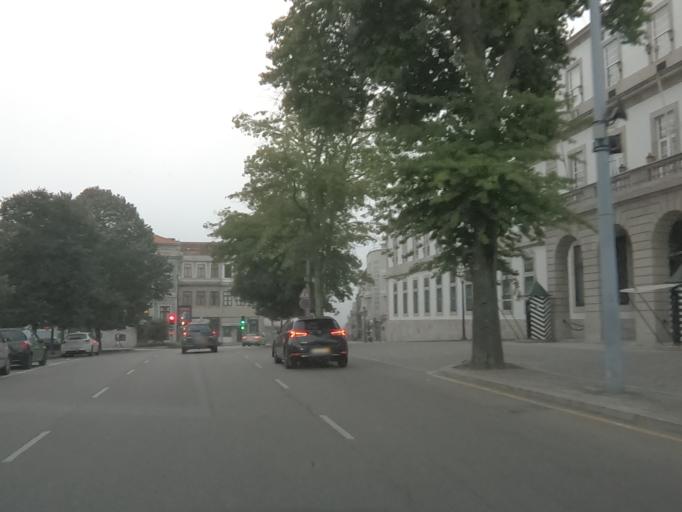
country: PT
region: Porto
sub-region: Porto
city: Porto
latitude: 41.1537
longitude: -8.6151
